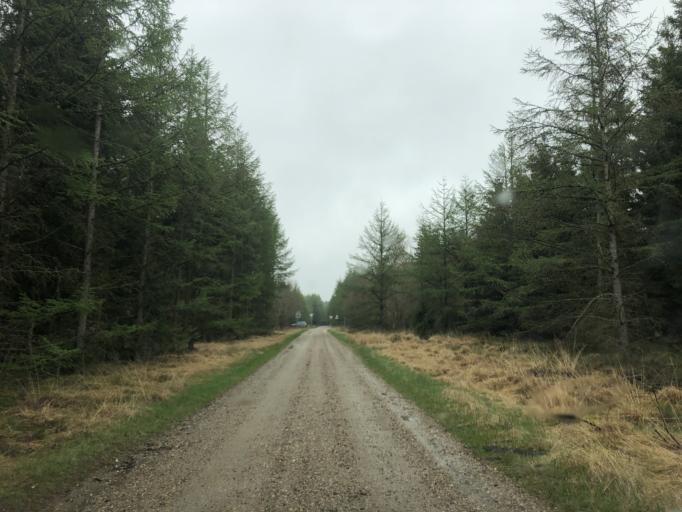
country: DK
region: Central Jutland
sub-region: Lemvig Kommune
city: Lemvig
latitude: 56.4612
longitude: 8.3988
